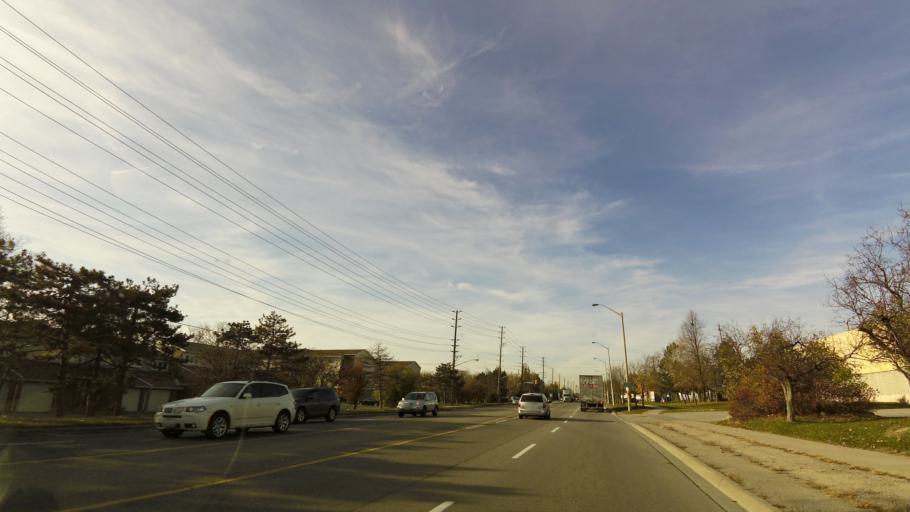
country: CA
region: Ontario
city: Brampton
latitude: 43.7264
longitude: -79.6962
